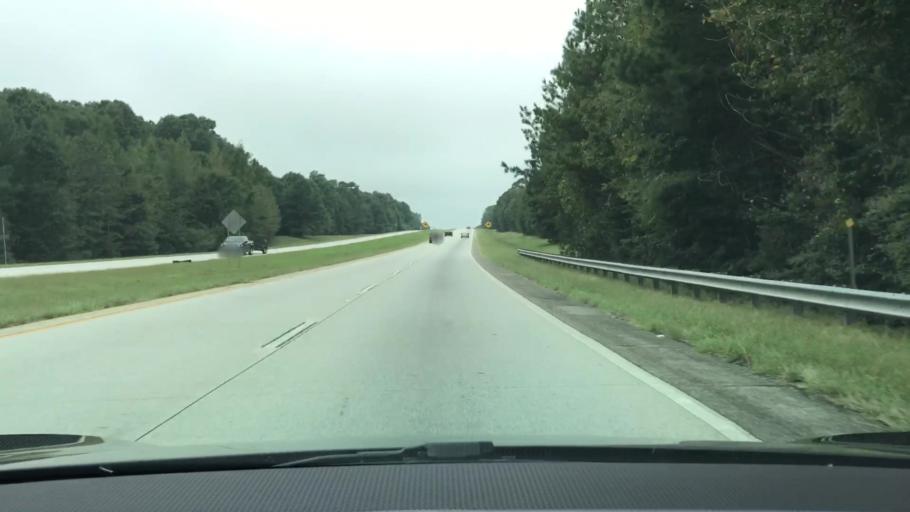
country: US
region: Georgia
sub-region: Barrow County
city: Statham
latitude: 33.9481
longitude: -83.5851
